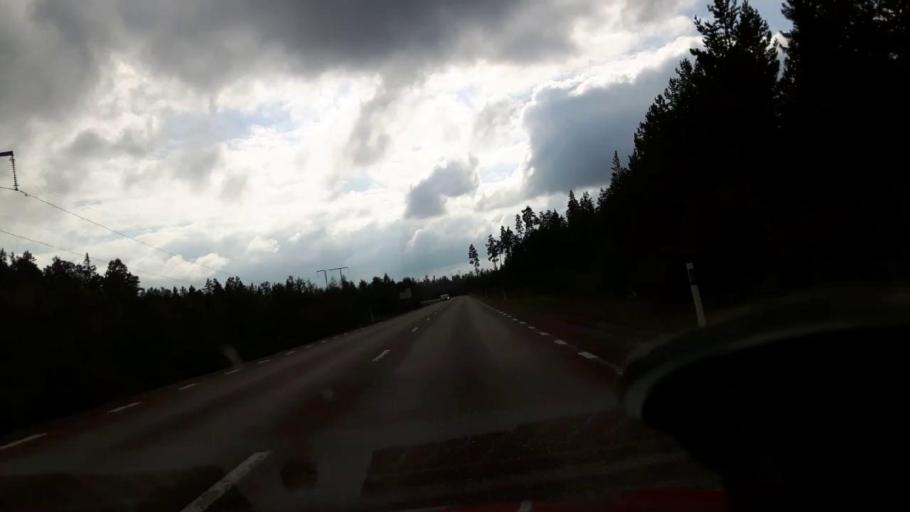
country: SE
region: Gaevleborg
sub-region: Soderhamns Kommun
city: Ljusne
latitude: 61.0938
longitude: 16.9547
